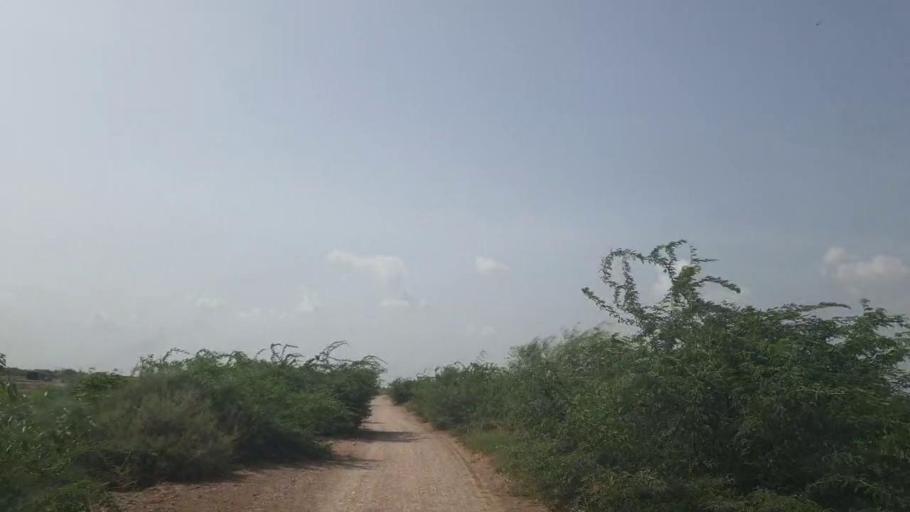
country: PK
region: Sindh
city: Tando Bago
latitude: 24.7687
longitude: 69.1313
